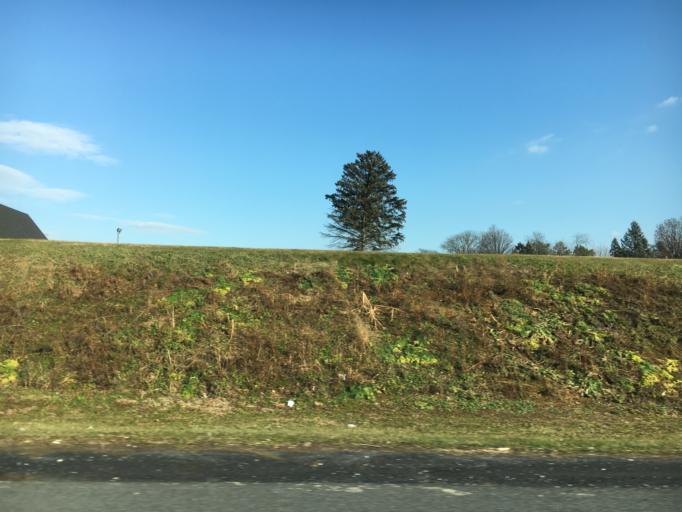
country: US
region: Pennsylvania
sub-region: Lehigh County
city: Stiles
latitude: 40.6575
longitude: -75.5073
